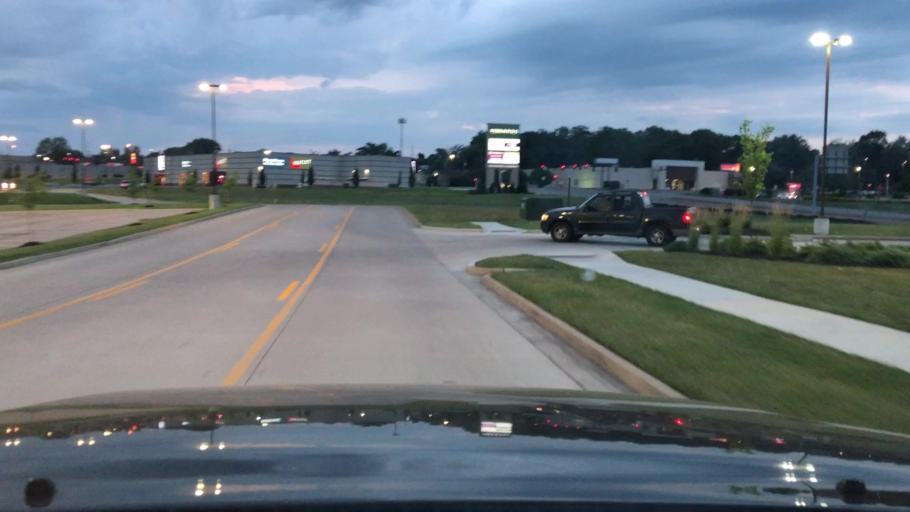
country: US
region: Missouri
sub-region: Saint Louis County
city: Saint Ann
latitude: 38.7355
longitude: -90.4007
